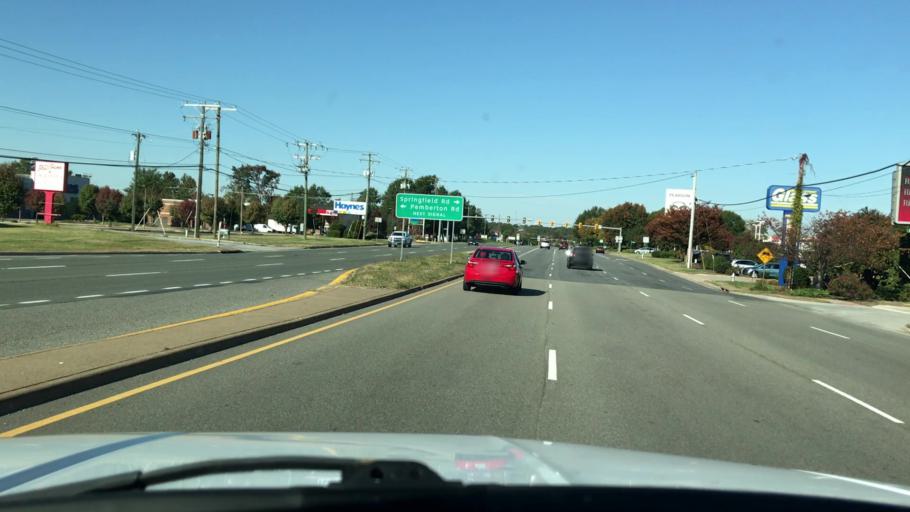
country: US
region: Virginia
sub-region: Henrico County
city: Laurel
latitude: 37.6399
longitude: -77.5584
